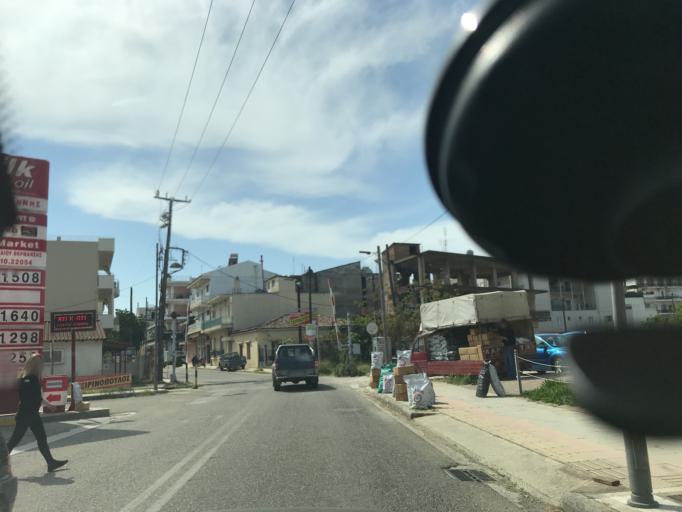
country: GR
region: West Greece
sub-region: Nomos Ileias
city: Pyrgos
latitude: 37.6786
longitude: 21.4402
